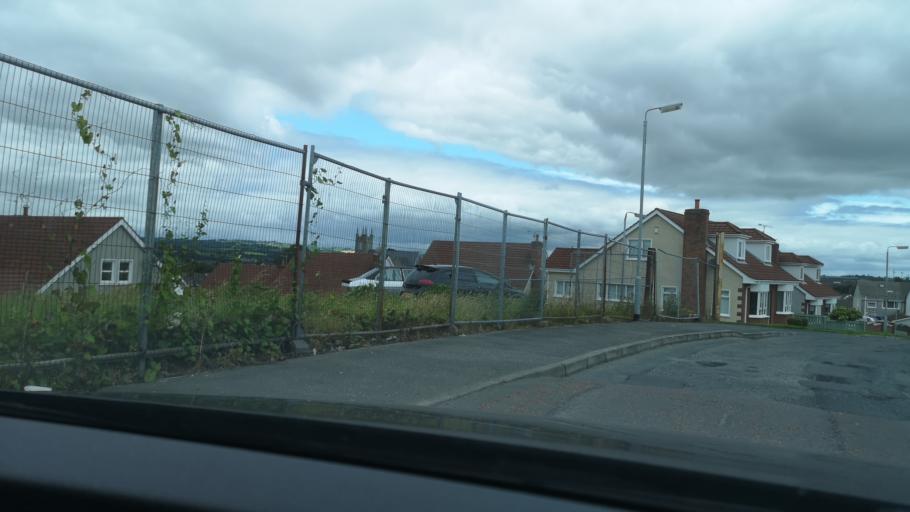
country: GB
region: Northern Ireland
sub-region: Newry and Mourne District
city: Newry
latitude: 54.1748
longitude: -6.3285
